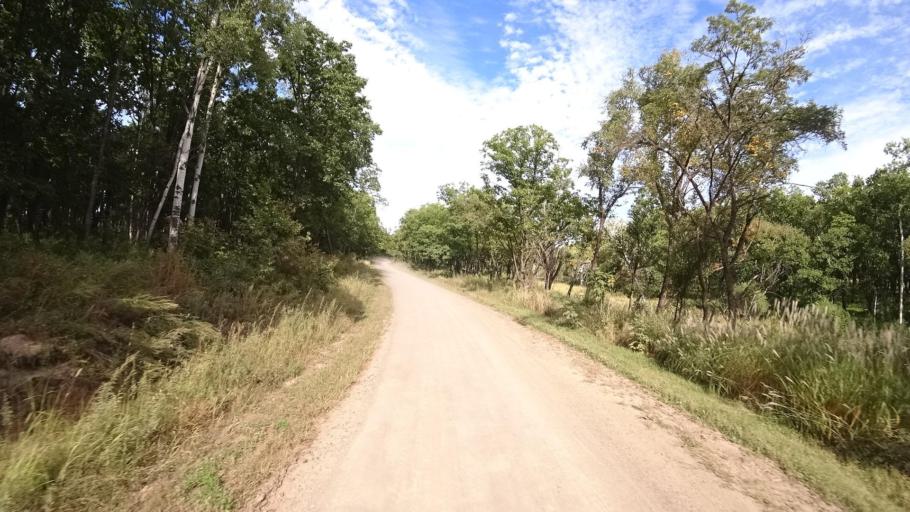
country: RU
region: Primorskiy
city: Yakovlevka
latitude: 44.3934
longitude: 133.5524
